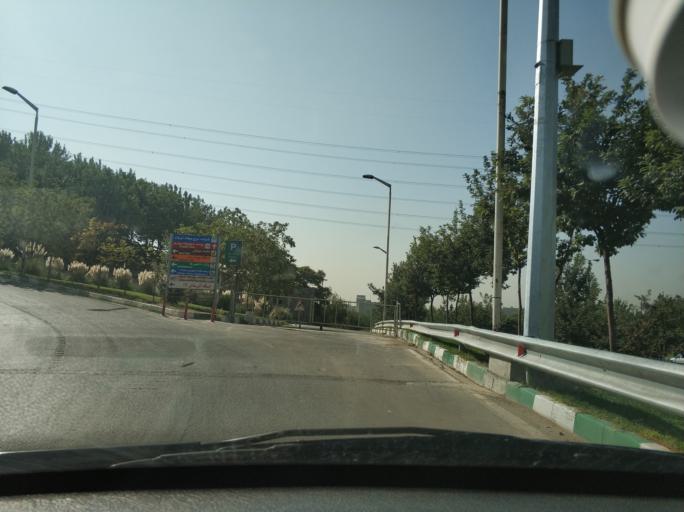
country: IR
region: Tehran
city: Tehran
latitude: 35.7436
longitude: 51.3700
